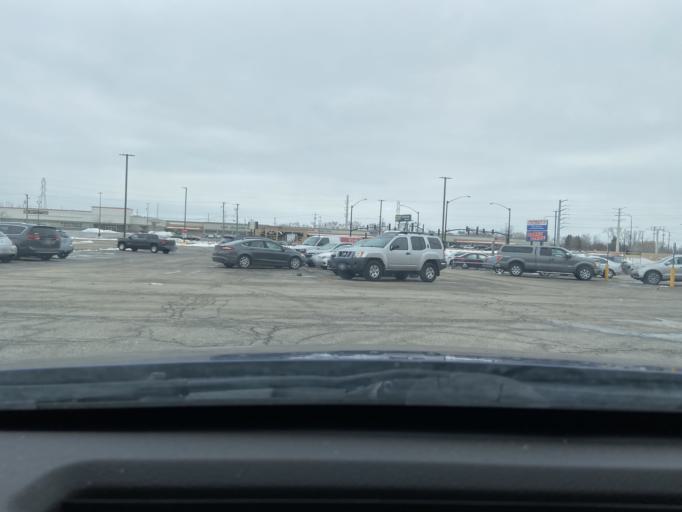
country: US
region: Illinois
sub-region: Lake County
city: Venetian Village
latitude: 42.3818
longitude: -88.0600
